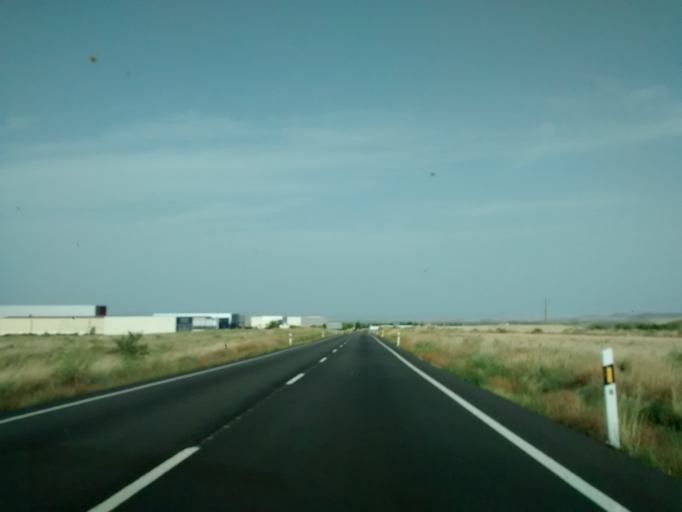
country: ES
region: Aragon
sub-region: Provincia de Zaragoza
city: Albeta
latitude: 41.8306
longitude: -1.4904
